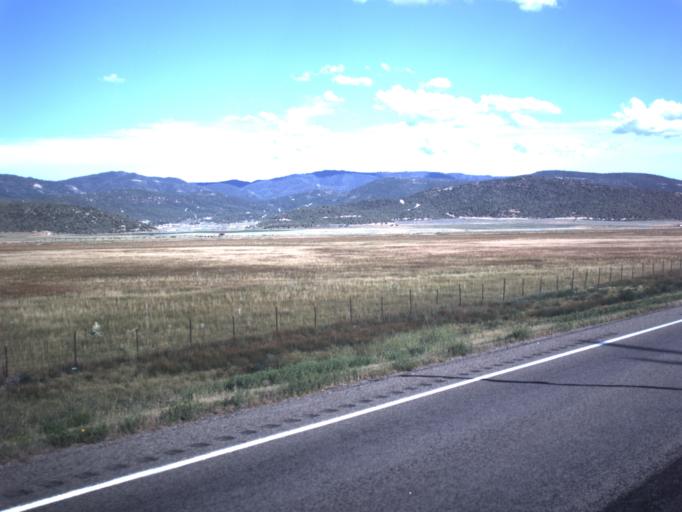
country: US
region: Utah
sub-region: Sanpete County
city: Fairview
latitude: 39.7957
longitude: -111.4990
